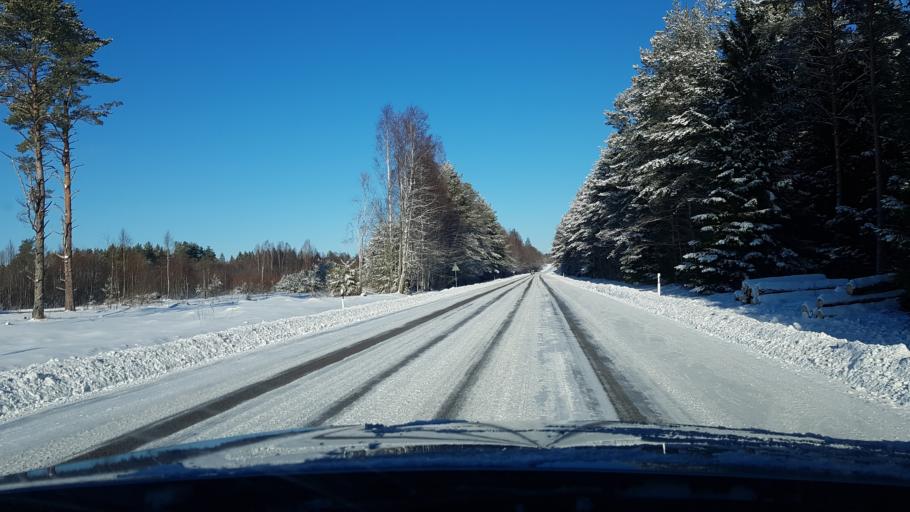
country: EE
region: Hiiumaa
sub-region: Kaerdla linn
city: Kardla
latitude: 58.9096
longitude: 22.7920
